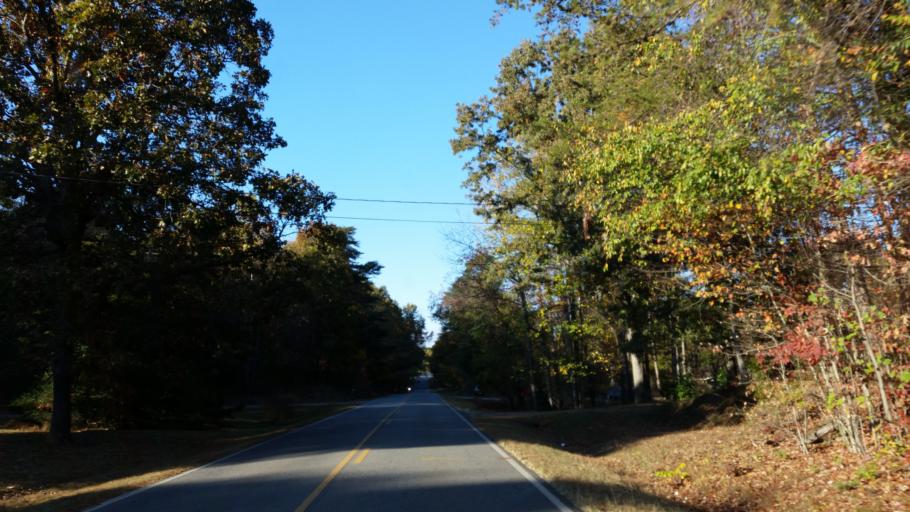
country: US
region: Georgia
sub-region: Gilmer County
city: Ellijay
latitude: 34.6091
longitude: -84.4644
